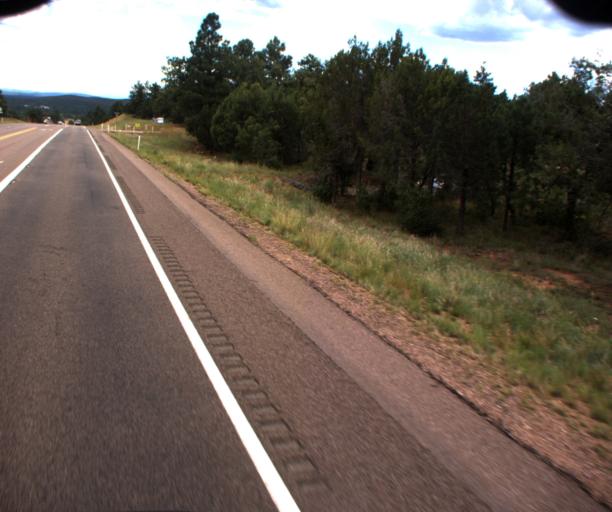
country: US
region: Arizona
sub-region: Navajo County
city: Linden
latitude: 34.2908
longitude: -110.1788
